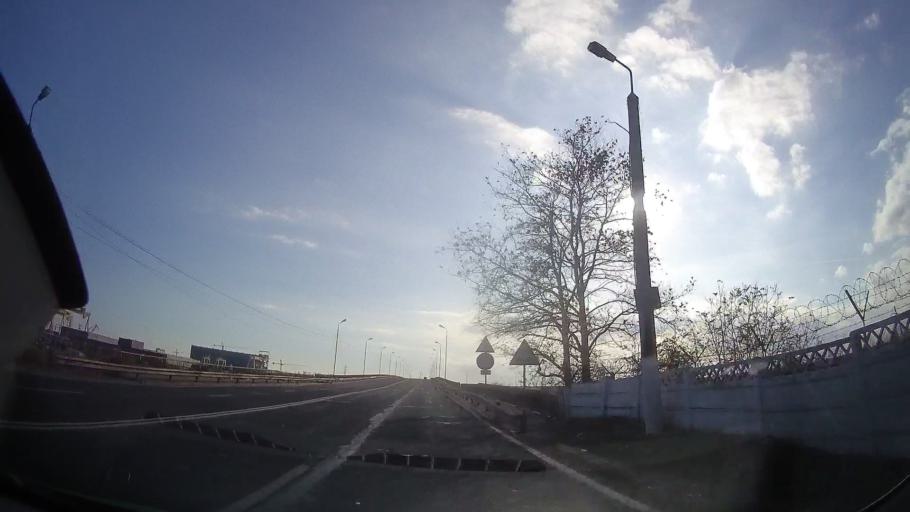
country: RO
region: Constanta
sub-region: Municipiul Mangalia
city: Mangalia
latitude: 43.8064
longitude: 28.5609
